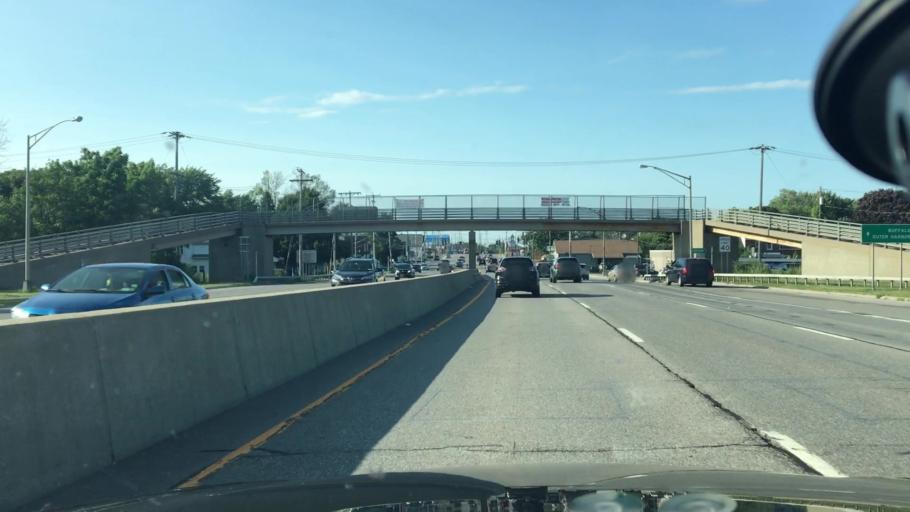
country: US
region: New York
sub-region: Erie County
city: Blasdell
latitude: 42.7929
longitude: -78.8468
